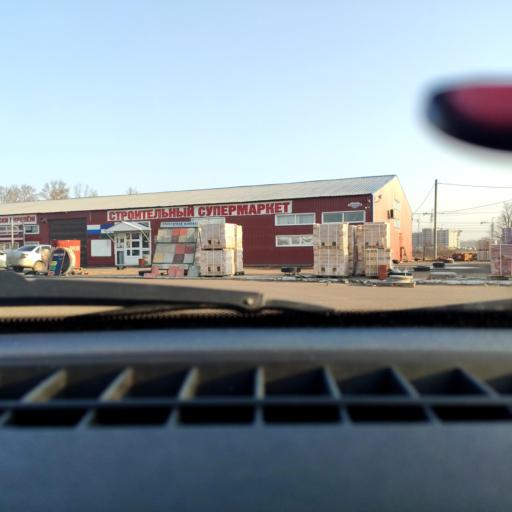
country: RU
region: Bashkortostan
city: Ufa
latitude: 54.7758
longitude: 55.9524
